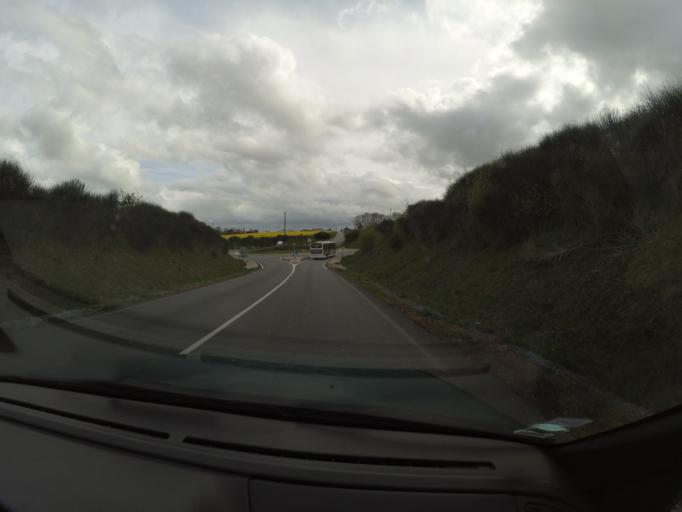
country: FR
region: Pays de la Loire
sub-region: Departement de Maine-et-Loire
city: Lire
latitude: 47.3311
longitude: -1.1680
